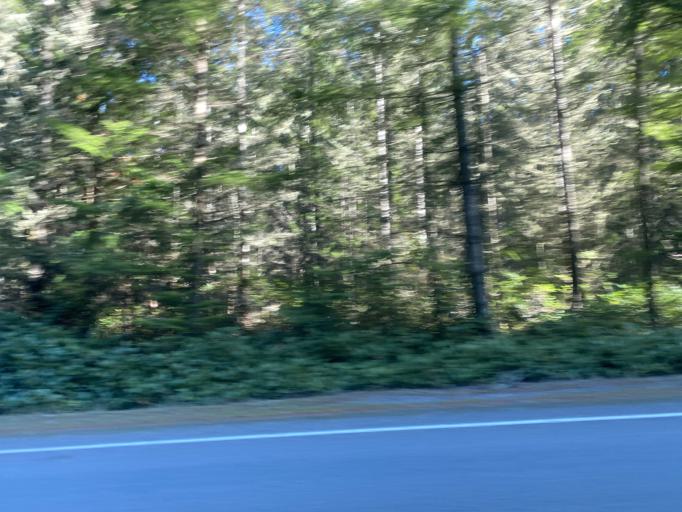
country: US
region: Washington
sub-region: Island County
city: Langley
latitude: 48.0258
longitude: -122.4227
